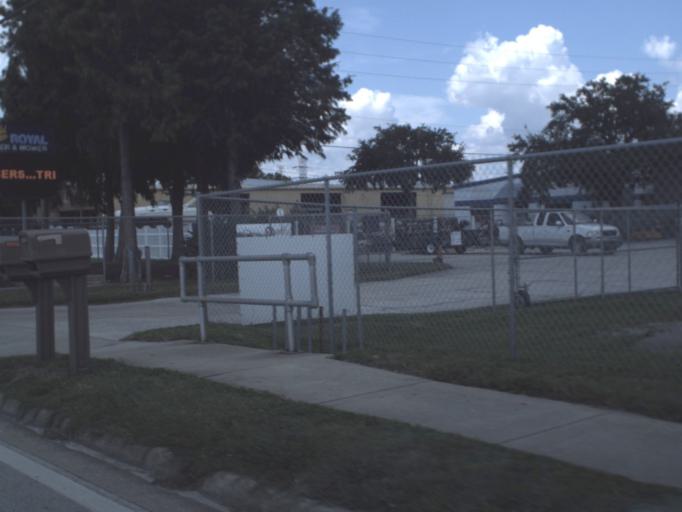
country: US
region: Florida
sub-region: Pinellas County
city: Pinellas Park
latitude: 27.8703
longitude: -82.7001
